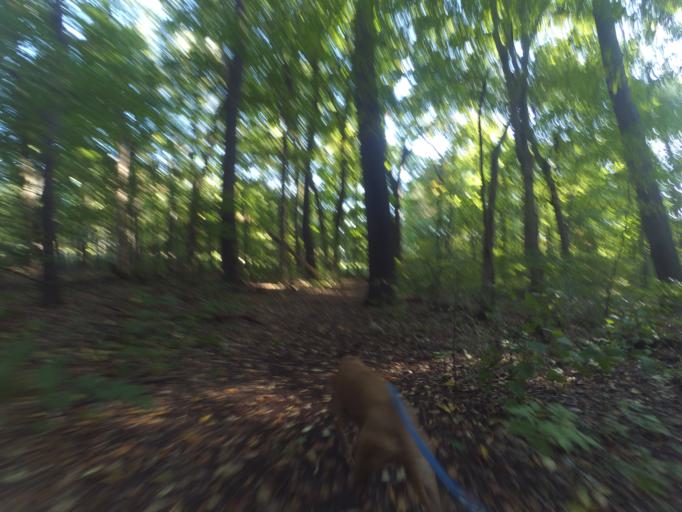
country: US
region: Ohio
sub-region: Portage County
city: Kent
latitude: 41.1562
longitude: -81.3721
